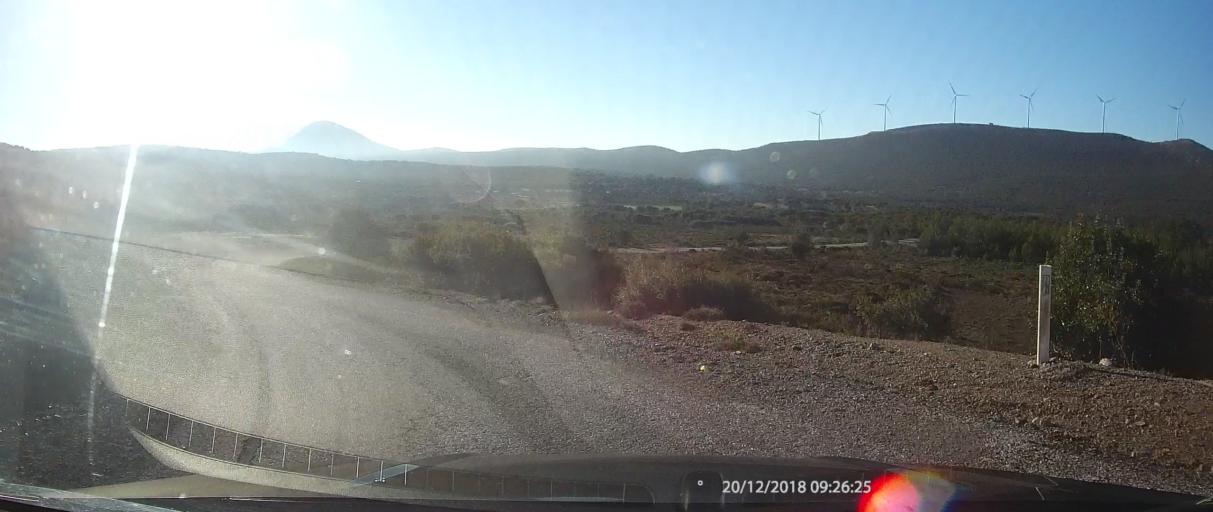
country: GR
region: Peloponnese
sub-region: Nomos Lakonias
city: Molaoi
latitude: 36.9633
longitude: 22.8752
